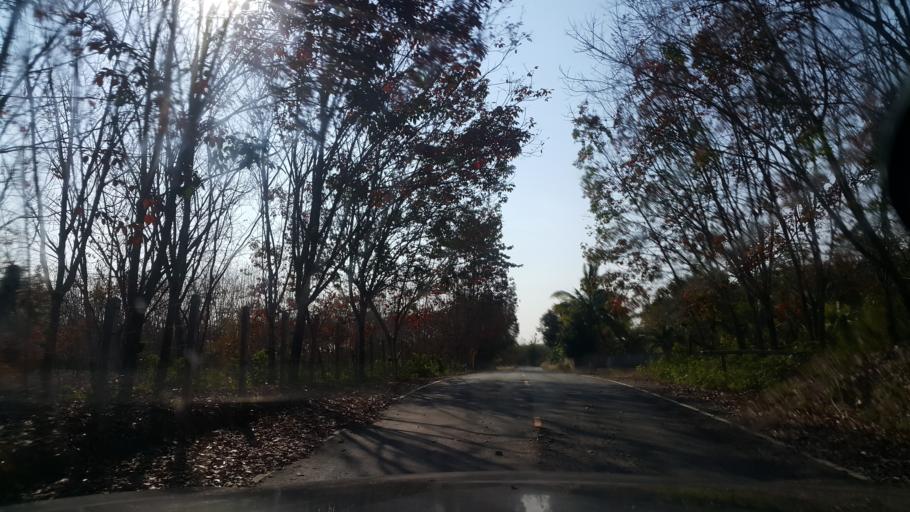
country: TH
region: Loei
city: Chiang Khan
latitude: 17.8492
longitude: 101.6013
